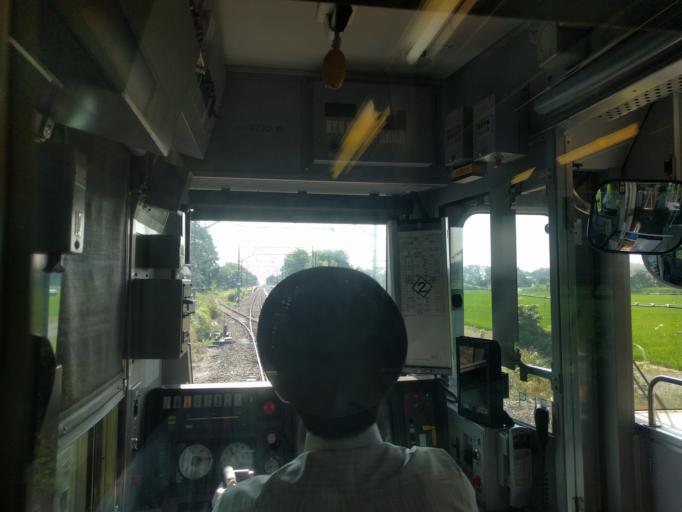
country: JP
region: Fukushima
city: Inawashiro
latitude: 37.5531
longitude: 140.0514
